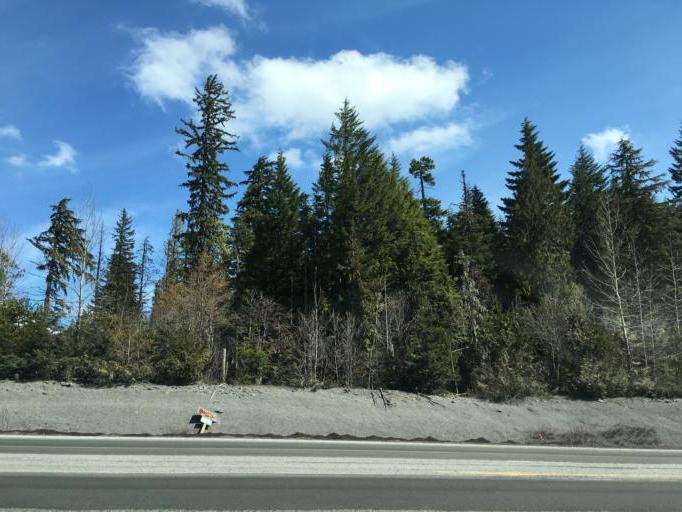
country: US
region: Oregon
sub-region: Clackamas County
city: Mount Hood Village
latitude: 45.2863
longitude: -121.7282
